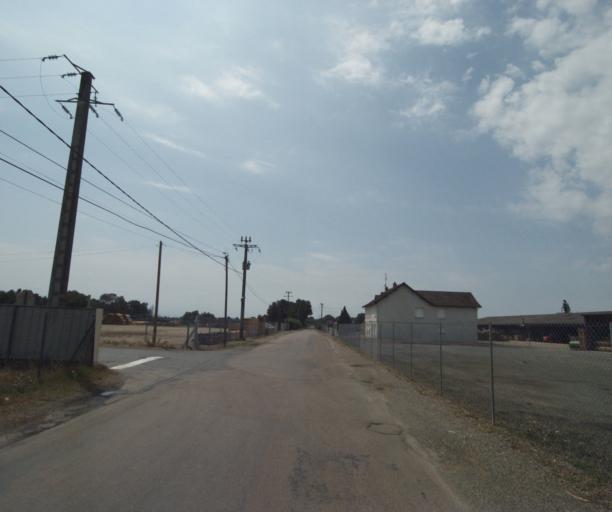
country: FR
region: Bourgogne
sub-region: Departement de Saone-et-Loire
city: Gueugnon
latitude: 46.5887
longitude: 4.0531
